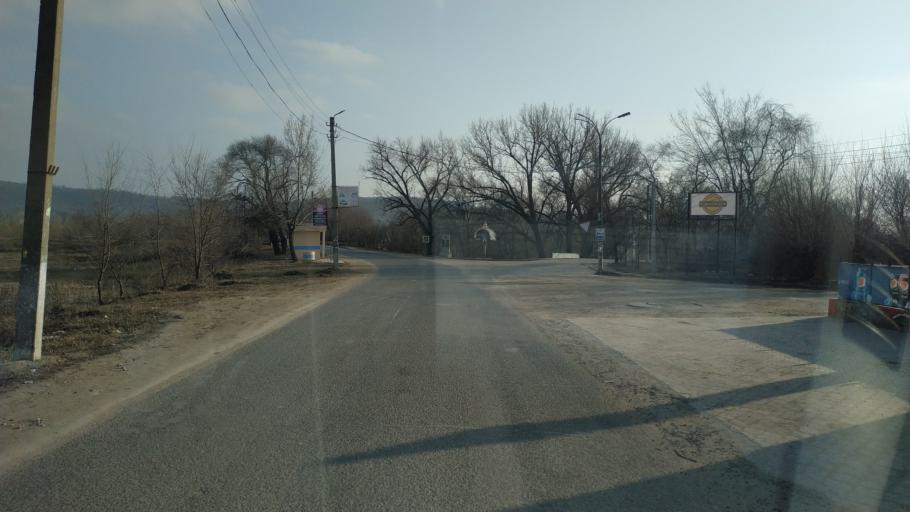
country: MD
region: Hincesti
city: Dancu
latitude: 46.7658
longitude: 28.3460
